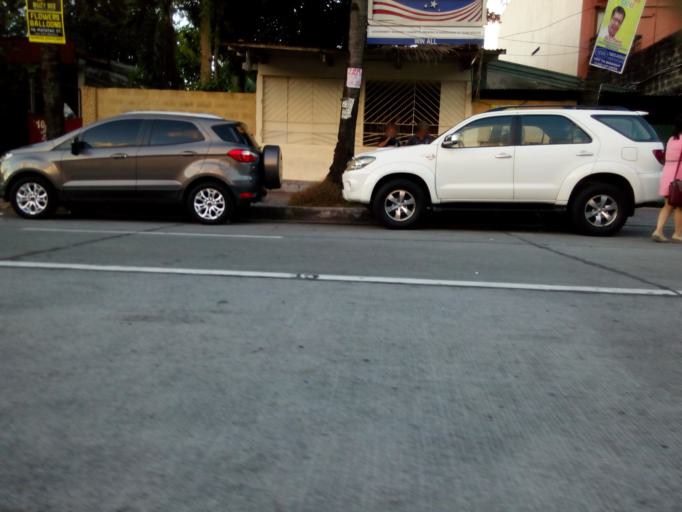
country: PH
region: Metro Manila
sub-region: Quezon City
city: Quezon City
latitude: 14.6461
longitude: 121.0602
